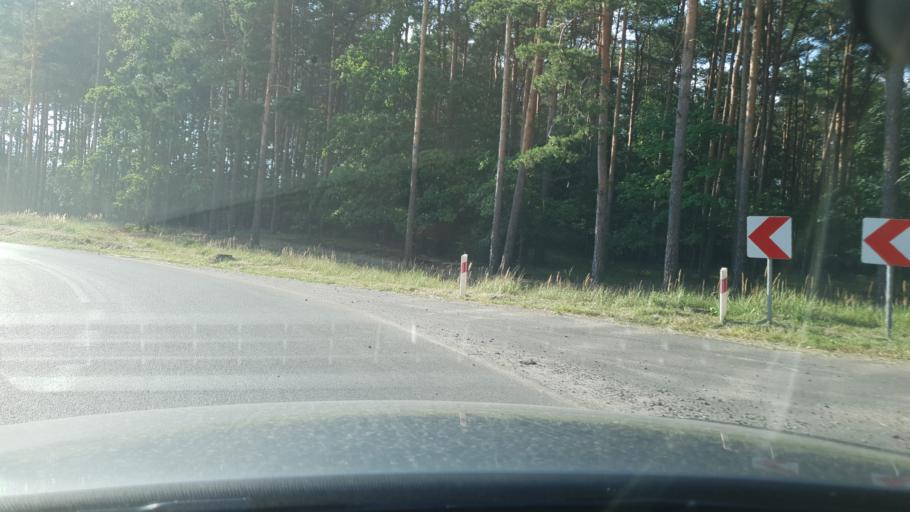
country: PL
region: Kujawsko-Pomorskie
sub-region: Grudziadz
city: Grudziadz
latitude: 53.4455
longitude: 18.7522
